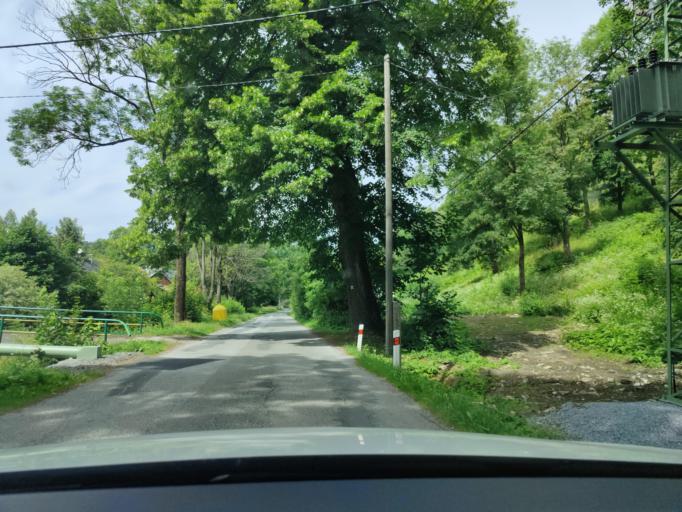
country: CZ
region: Olomoucky
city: Zlate Hory
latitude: 50.2340
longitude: 17.3451
